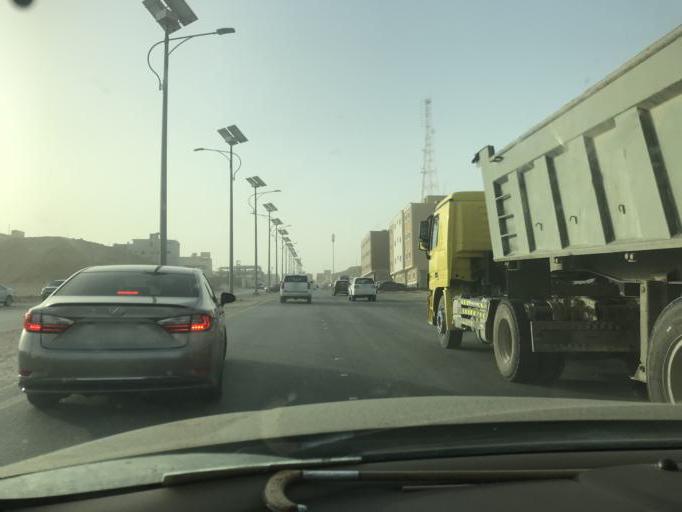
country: SA
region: Ar Riyad
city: Riyadh
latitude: 24.8419
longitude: 46.6661
